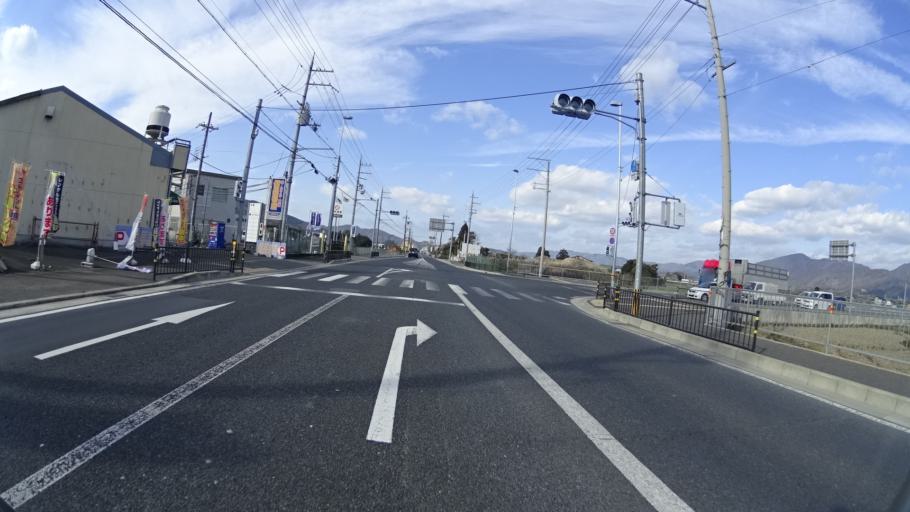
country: JP
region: Kyoto
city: Kameoka
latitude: 35.0216
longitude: 135.5600
